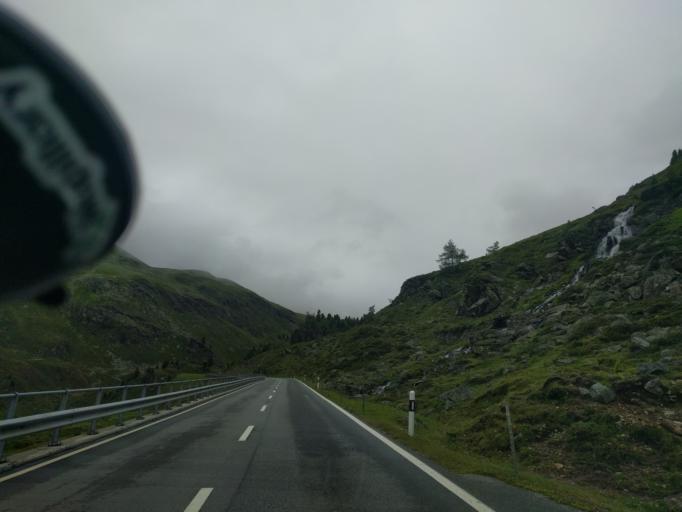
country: CH
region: Grisons
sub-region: Praettigau/Davos District
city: Davos
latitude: 46.7814
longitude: 9.9234
